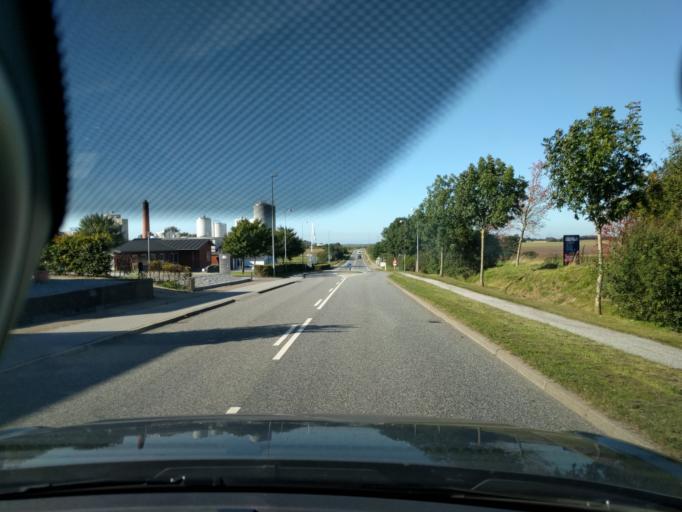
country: DK
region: North Denmark
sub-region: Vesthimmerland Kommune
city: Alestrup
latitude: 56.7101
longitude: 9.6236
